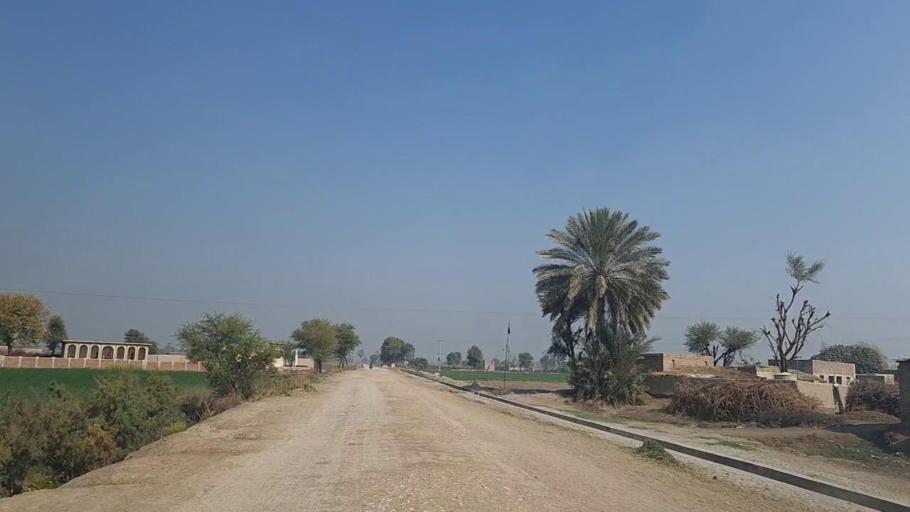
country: PK
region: Sindh
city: Nawabshah
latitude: 26.2282
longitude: 68.4907
